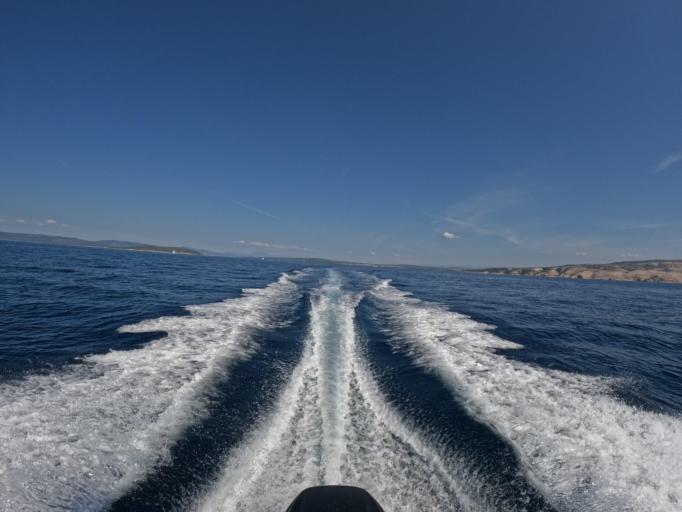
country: HR
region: Primorsko-Goranska
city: Punat
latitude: 44.9298
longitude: 14.6180
